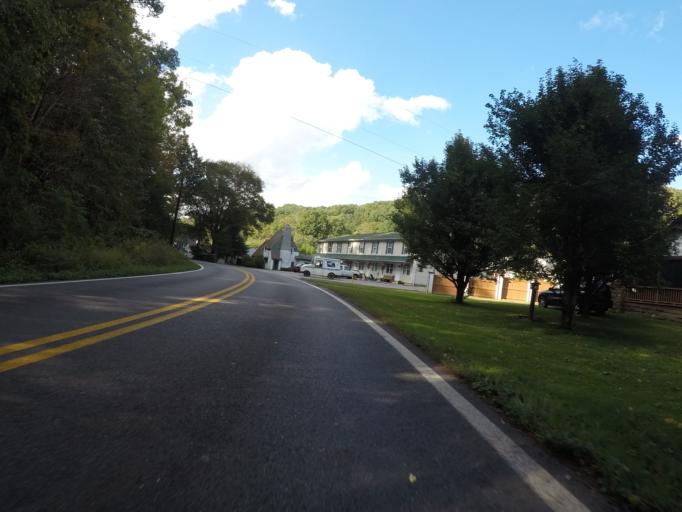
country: US
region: Ohio
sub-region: Lawrence County
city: Burlington
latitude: 38.3907
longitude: -82.5118
